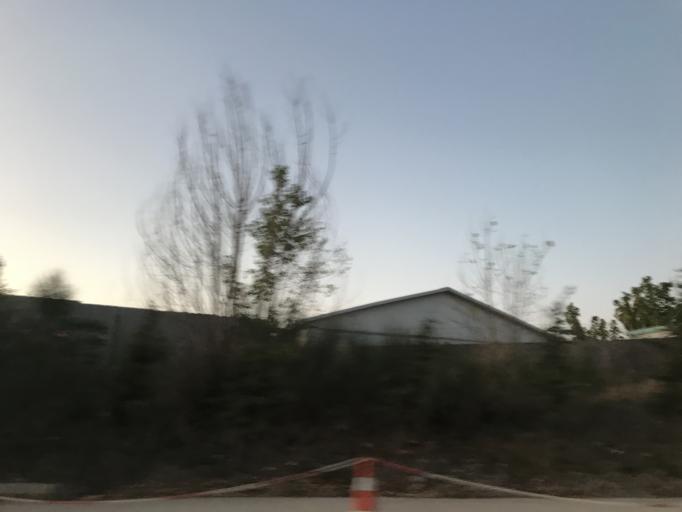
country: TR
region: Istanbul
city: Icmeler
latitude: 40.8405
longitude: 29.3106
